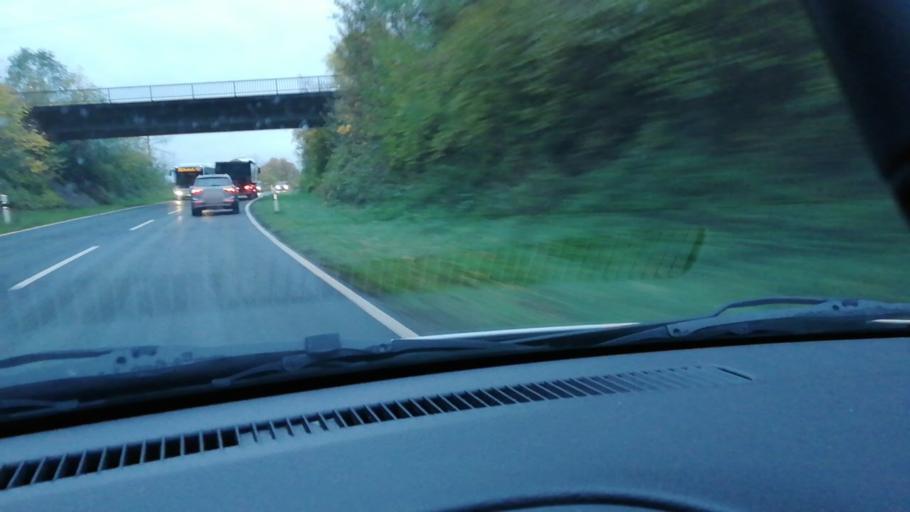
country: DE
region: Bavaria
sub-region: Regierungsbezirk Unterfranken
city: Hosbach
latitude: 50.0141
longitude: 9.2193
